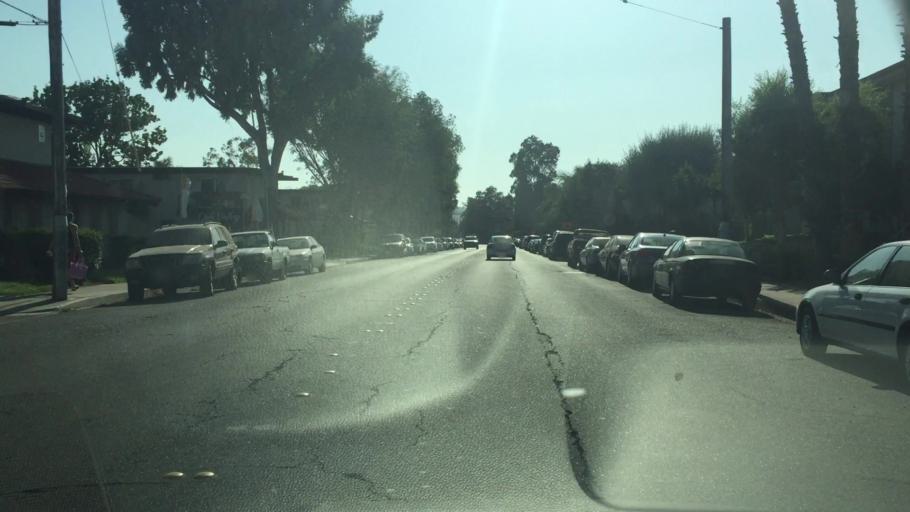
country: US
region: California
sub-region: San Diego County
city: El Cajon
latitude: 32.7929
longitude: -116.9463
